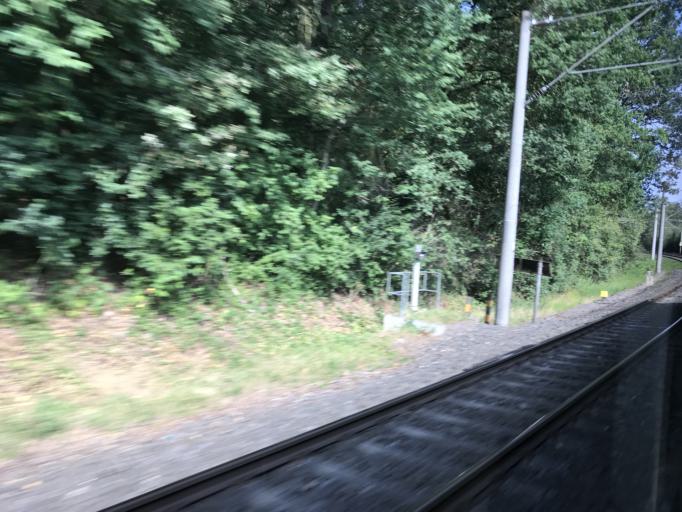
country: DE
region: Hesse
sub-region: Regierungsbezirk Giessen
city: Runkel
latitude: 50.3836
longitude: 8.1328
